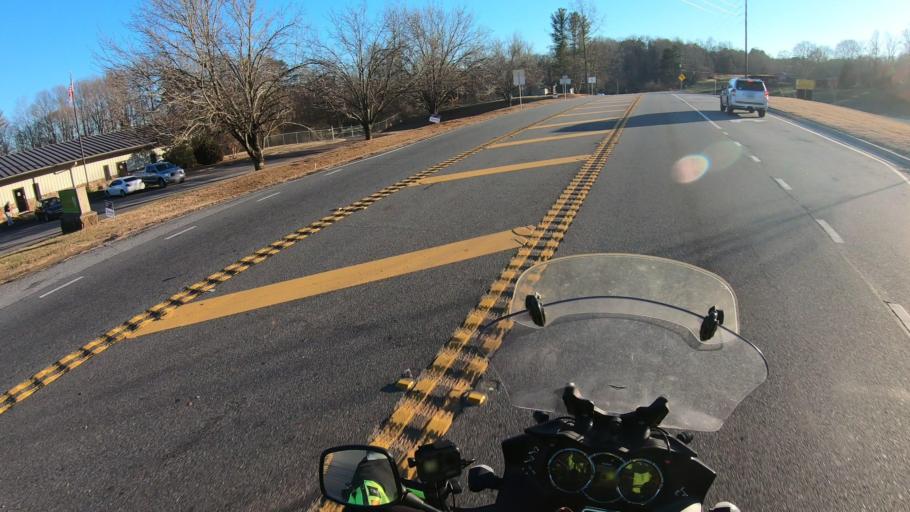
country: US
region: Georgia
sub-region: Lumpkin County
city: Dahlonega
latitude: 34.5691
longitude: -83.9697
